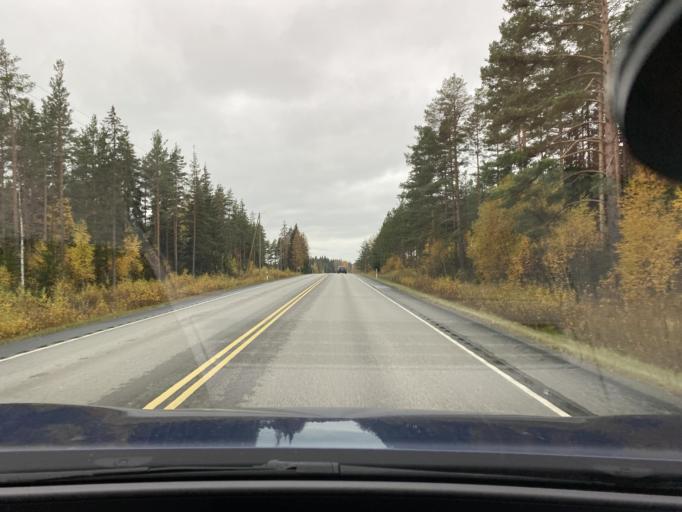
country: FI
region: Satakunta
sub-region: Rauma
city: Lappi
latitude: 61.1063
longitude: 21.9096
